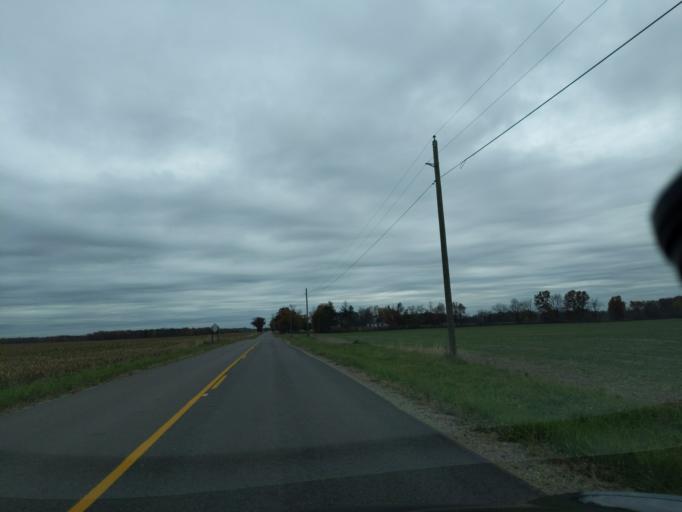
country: US
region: Michigan
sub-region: Eaton County
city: Eaton Rapids
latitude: 42.4356
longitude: -84.6104
